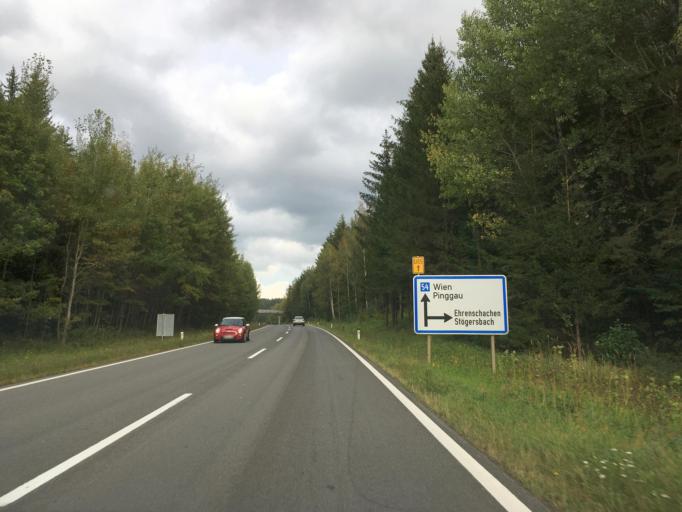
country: AT
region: Styria
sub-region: Politischer Bezirk Hartberg-Fuerstenfeld
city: Friedberg
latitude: 47.4173
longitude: 16.0440
